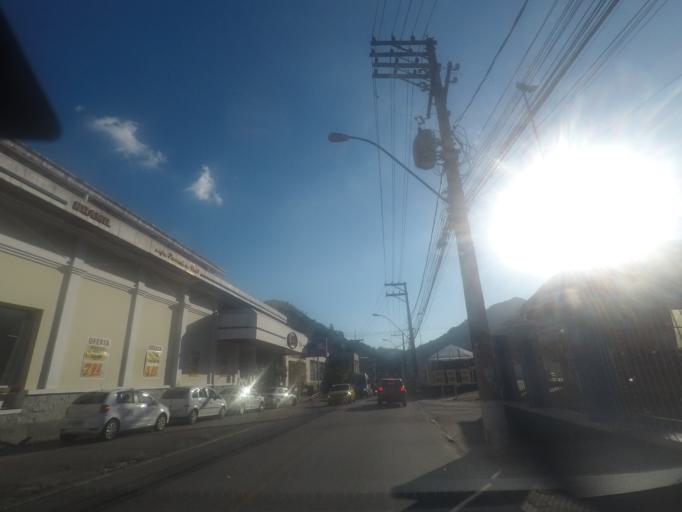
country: BR
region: Rio de Janeiro
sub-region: Petropolis
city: Petropolis
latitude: -22.4870
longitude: -43.1513
